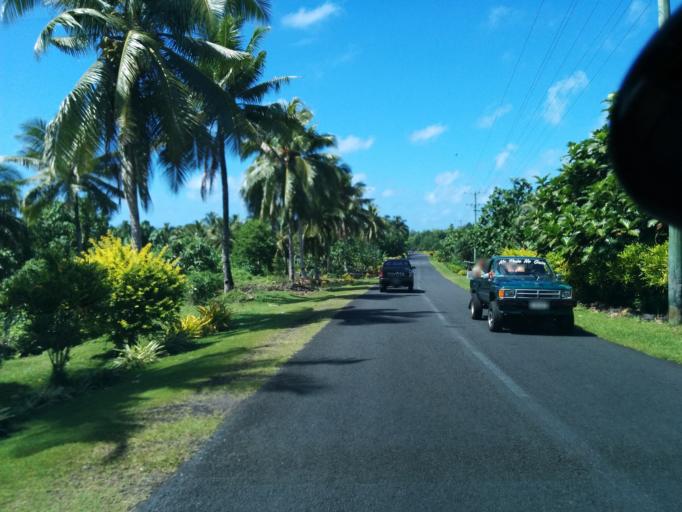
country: WS
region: Fa`asaleleaga
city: Safotulafai
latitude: -13.5831
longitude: -172.2165
